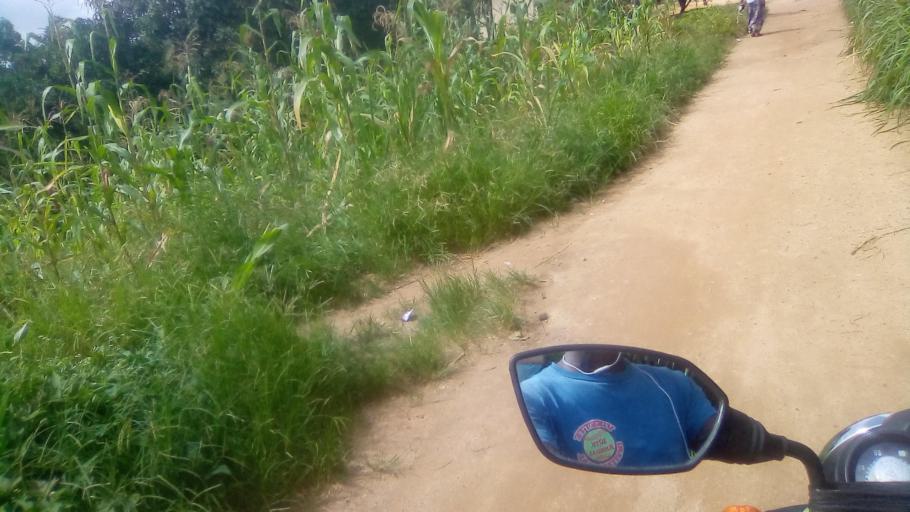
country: SL
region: Eastern Province
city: Kailahun
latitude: 8.2847
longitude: -10.5644
